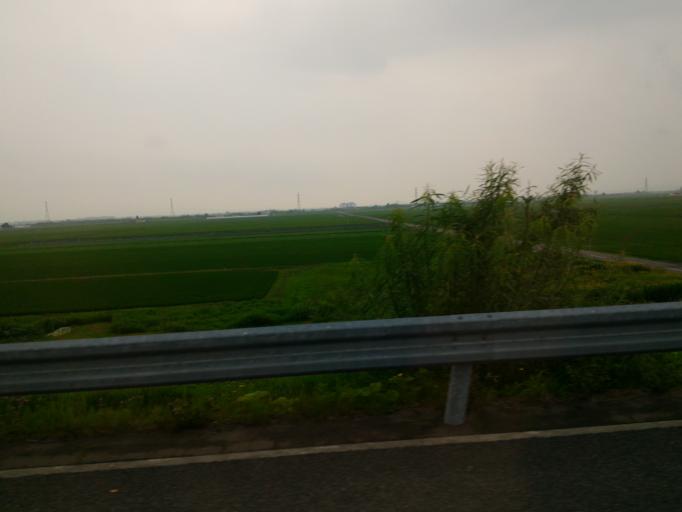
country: JP
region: Hokkaido
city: Fukagawa
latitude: 43.8027
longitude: 141.9275
